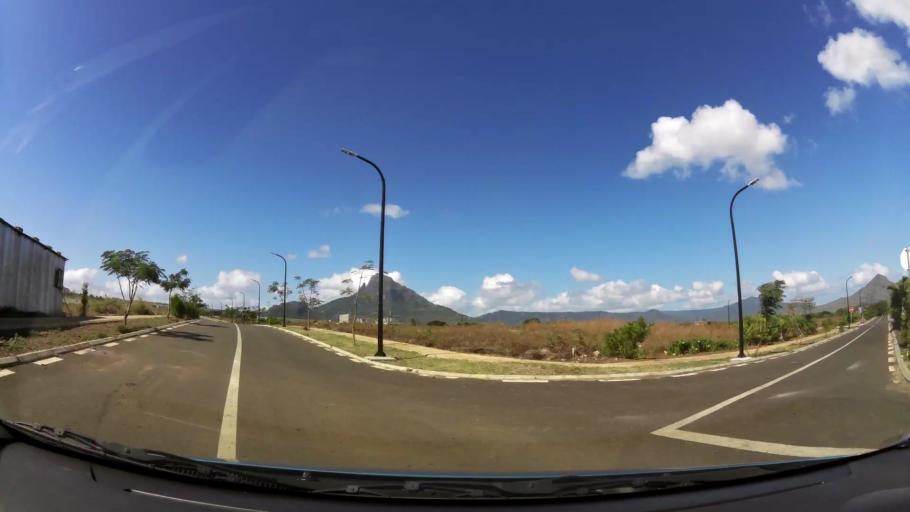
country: MU
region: Black River
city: Cascavelle
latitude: -20.2786
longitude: 57.3872
